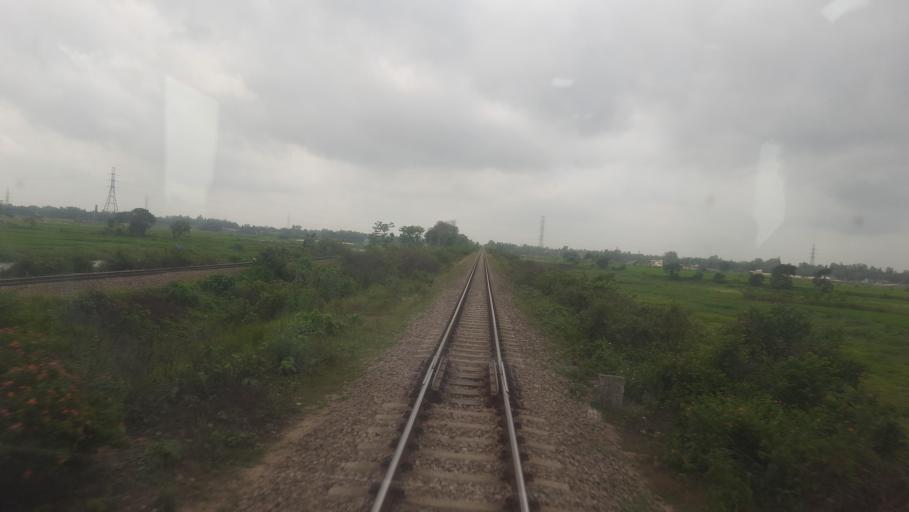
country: BD
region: Dhaka
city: Bhairab Bazar
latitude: 24.0464
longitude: 90.9670
